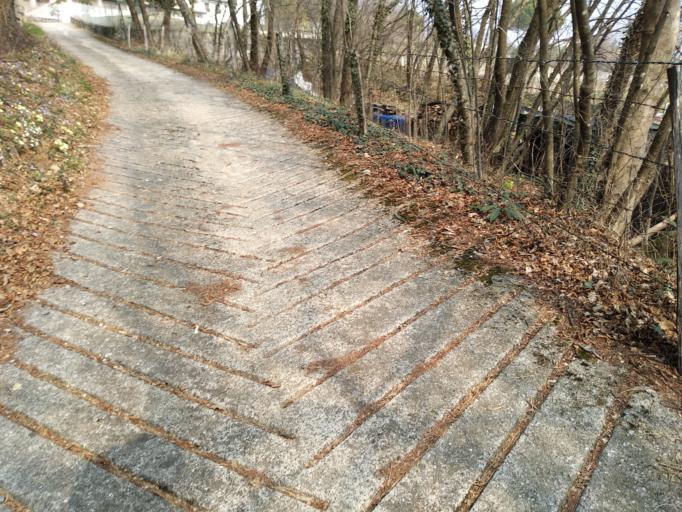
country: IT
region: Veneto
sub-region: Provincia di Vicenza
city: Santorso
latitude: 45.7412
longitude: 11.3999
